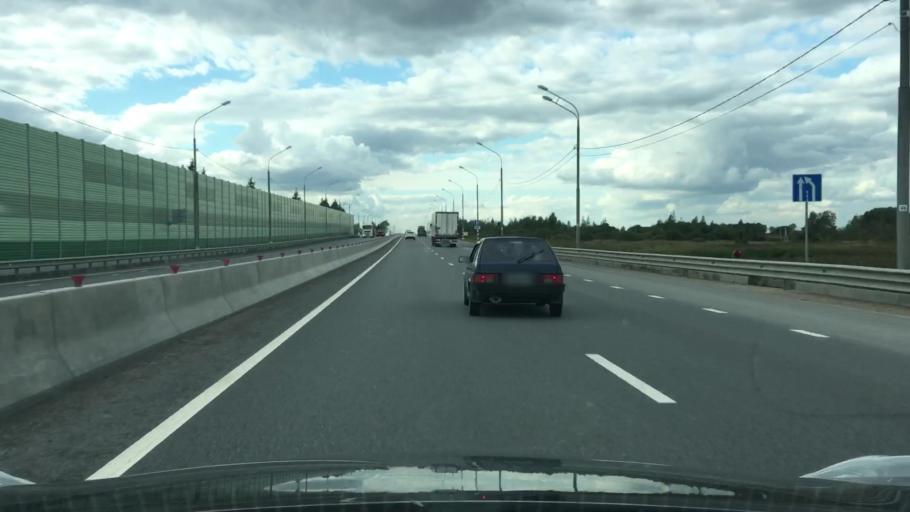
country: RU
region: Tverskaya
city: Tver
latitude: 56.7837
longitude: 35.9401
